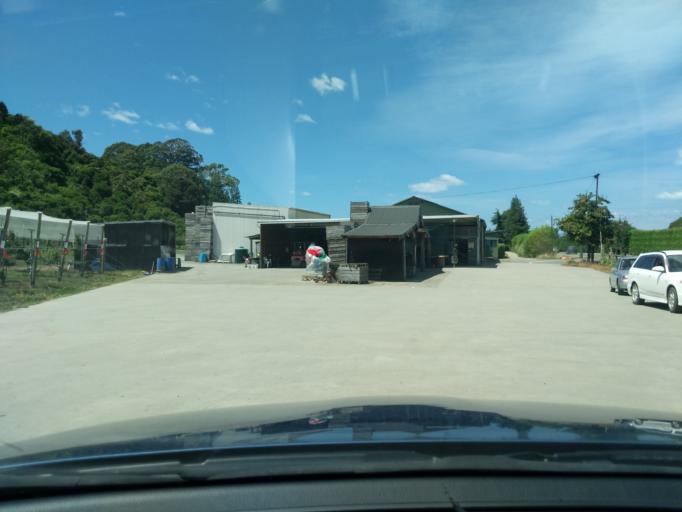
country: NZ
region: Tasman
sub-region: Tasman District
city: Motueka
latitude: -41.0592
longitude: 172.9708
